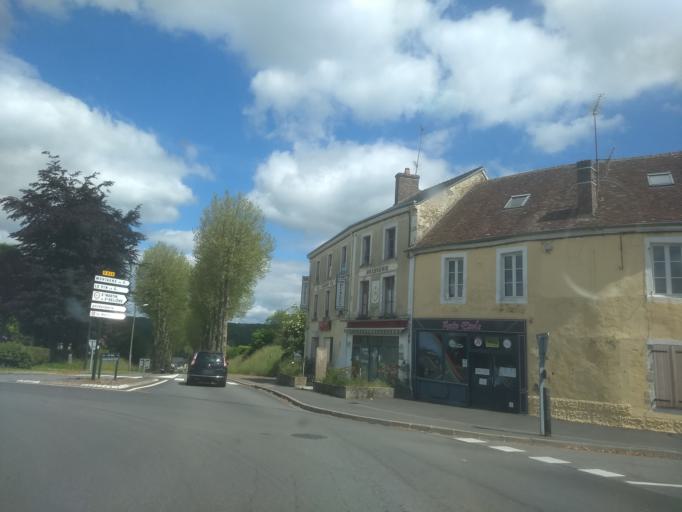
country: FR
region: Lower Normandy
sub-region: Departement de l'Orne
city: Belleme
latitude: 48.3767
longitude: 0.5564
